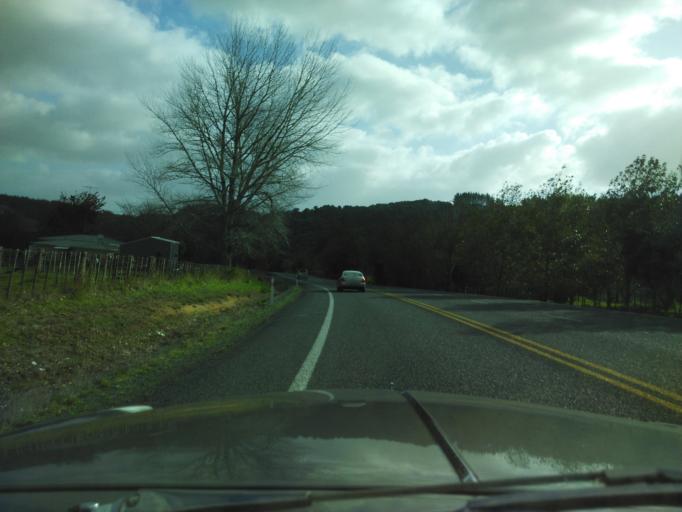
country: NZ
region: Auckland
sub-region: Auckland
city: Wellsford
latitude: -36.2125
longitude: 174.4788
